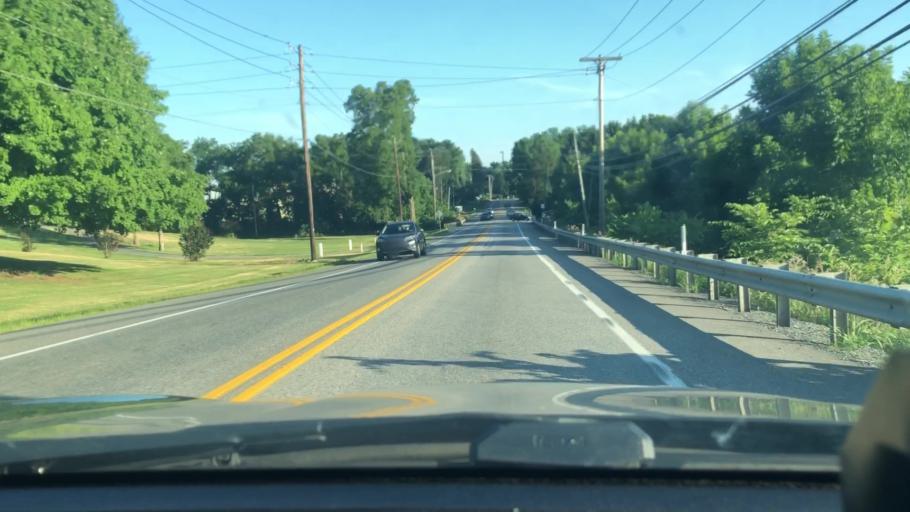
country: US
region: Pennsylvania
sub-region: Cumberland County
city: Mechanicsburg
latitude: 40.2380
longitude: -77.0075
